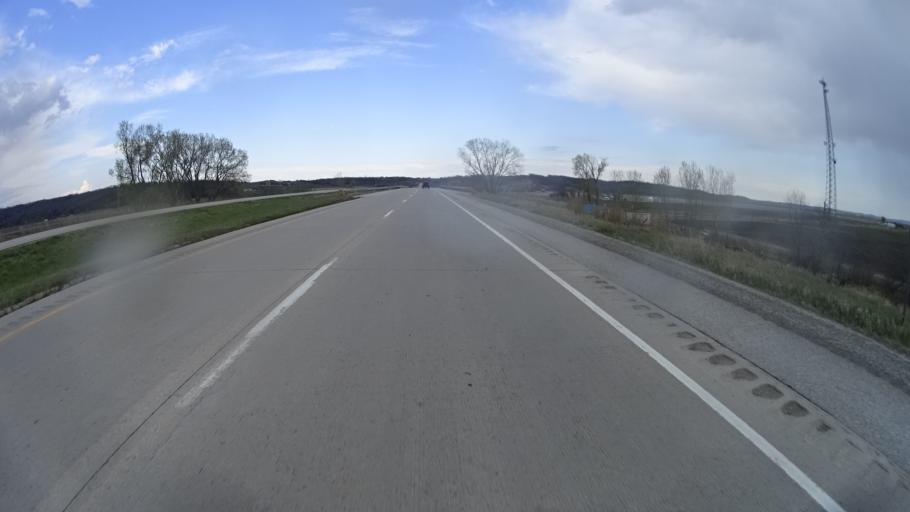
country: US
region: Iowa
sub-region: Mills County
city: Glenwood
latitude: 41.0459
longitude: -95.8103
